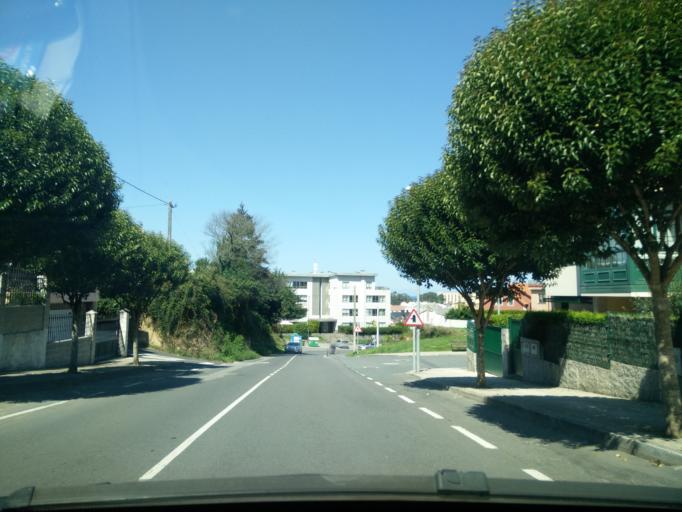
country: ES
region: Galicia
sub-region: Provincia da Coruna
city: Oleiros
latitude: 43.3434
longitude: -8.3430
